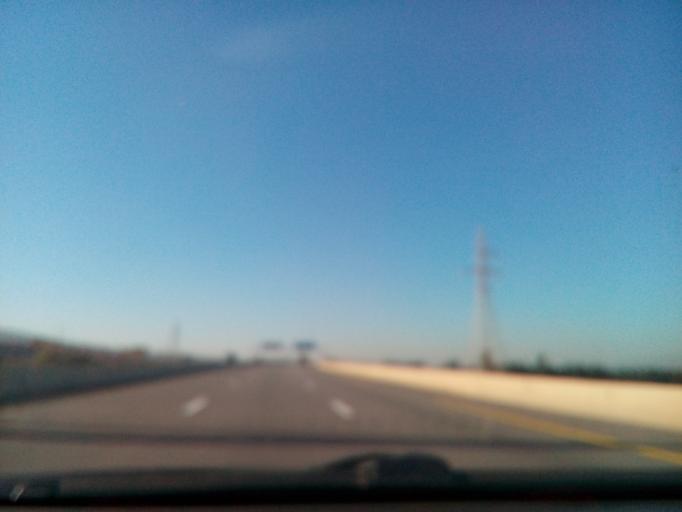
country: DZ
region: Chlef
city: Boukadir
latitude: 36.0245
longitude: 1.0569
